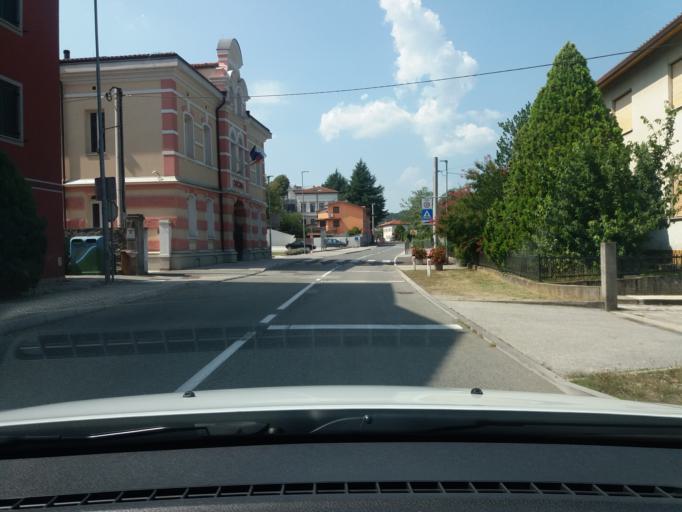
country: SI
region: Miren-Kostanjevica
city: Miren
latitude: 45.8922
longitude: 13.6064
